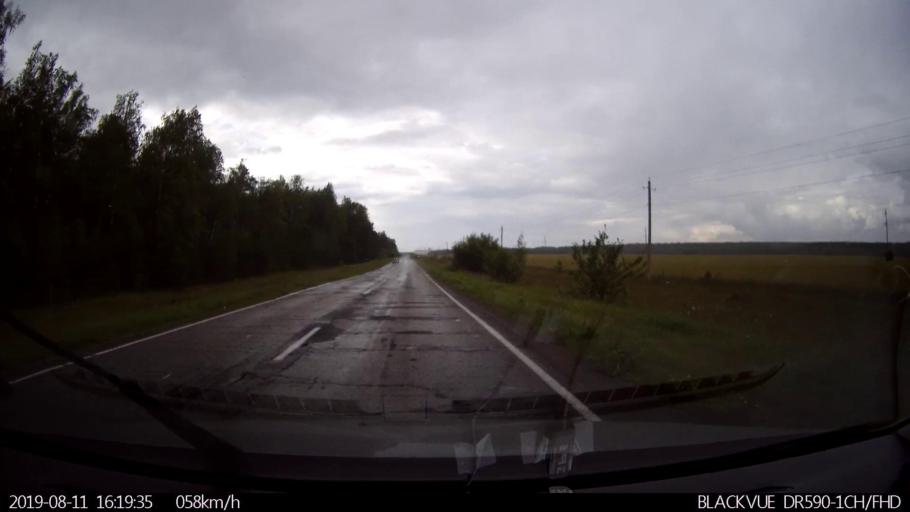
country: RU
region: Ulyanovsk
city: Mayna
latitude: 54.0649
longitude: 47.6067
